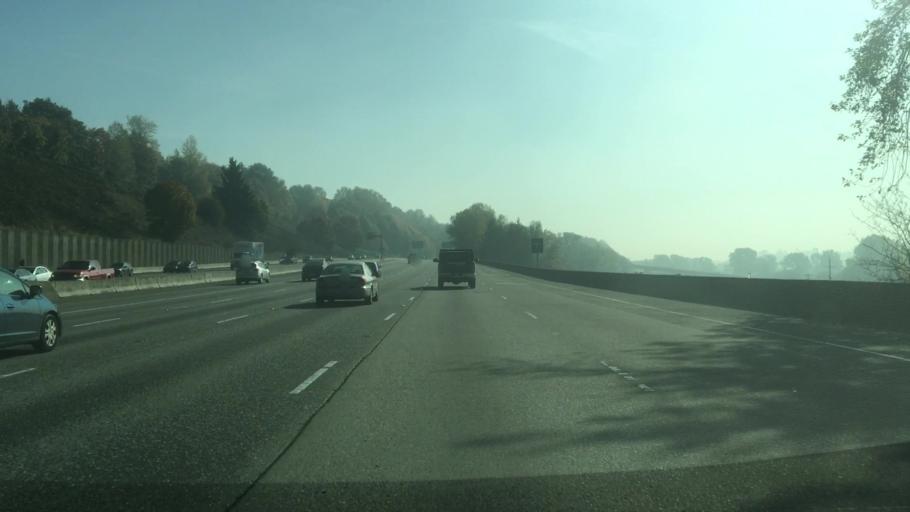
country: US
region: Washington
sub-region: King County
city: Tukwila
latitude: 47.4957
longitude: -122.2700
